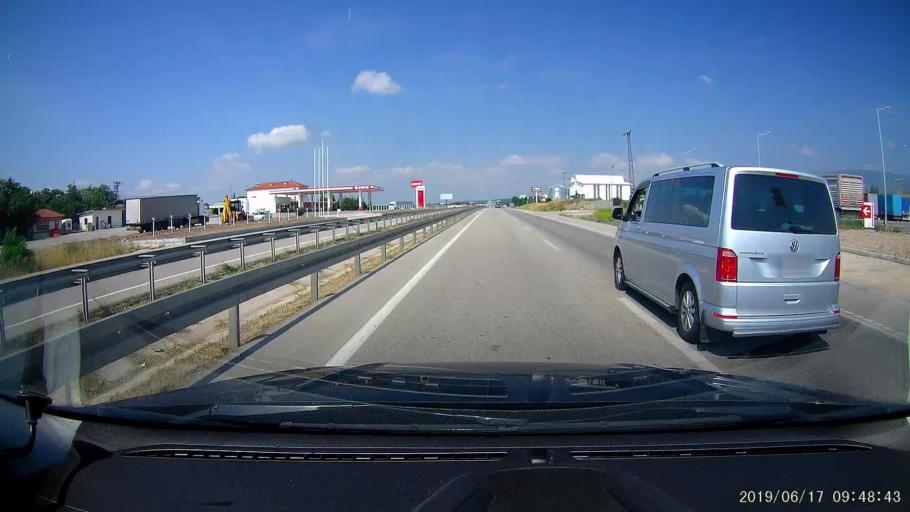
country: TR
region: Amasya
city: Merzifon
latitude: 40.8740
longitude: 35.5460
